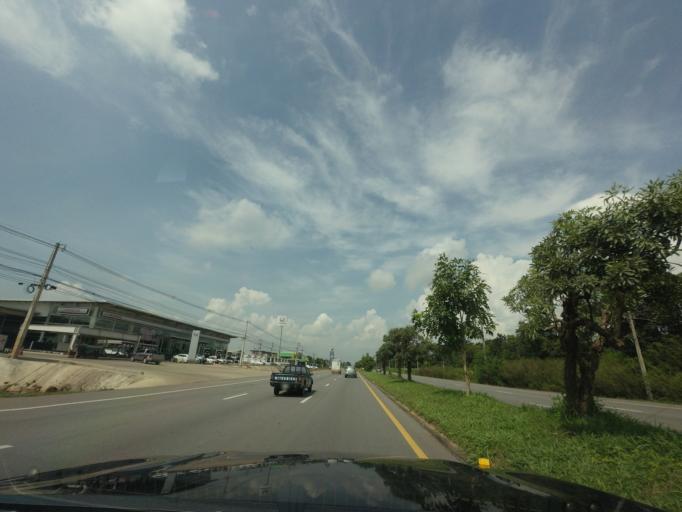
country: TH
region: Khon Kaen
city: Khon Kaen
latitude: 16.4507
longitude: 102.7422
